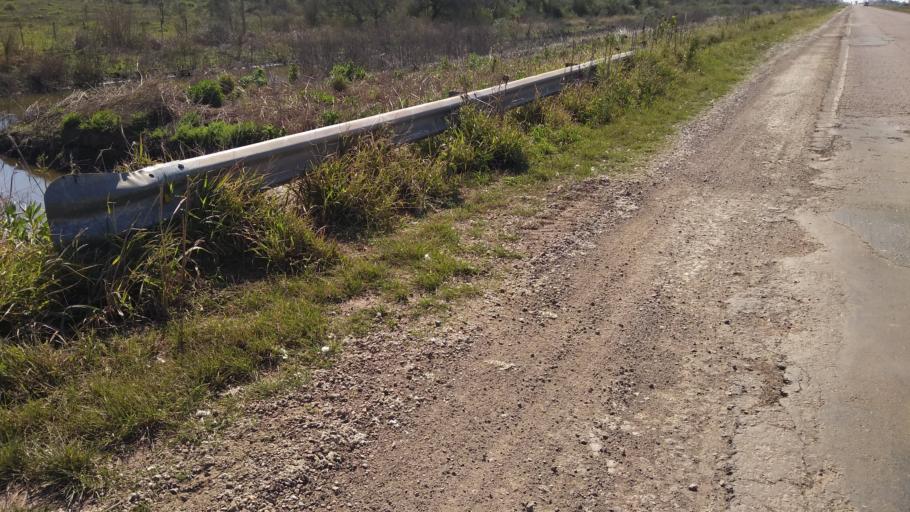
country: AR
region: Santiago del Estero
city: Los Juries
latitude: -28.6041
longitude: -61.5177
